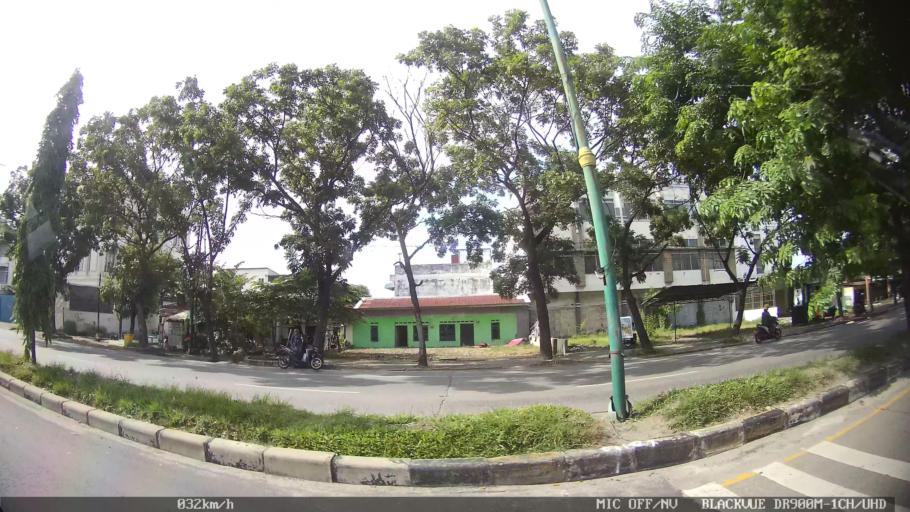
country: ID
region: North Sumatra
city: Medan
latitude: 3.6298
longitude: 98.6790
